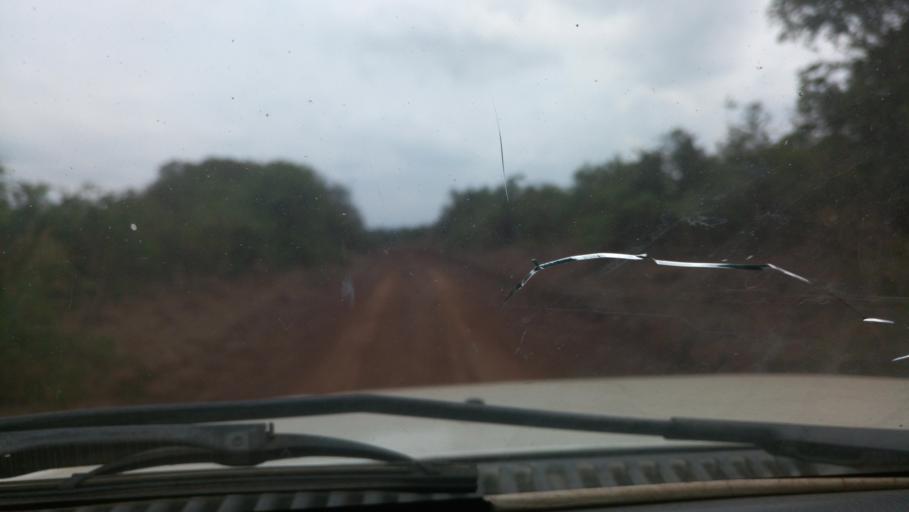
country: KE
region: Nairobi Area
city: Nairobi
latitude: -1.3567
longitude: 36.7815
